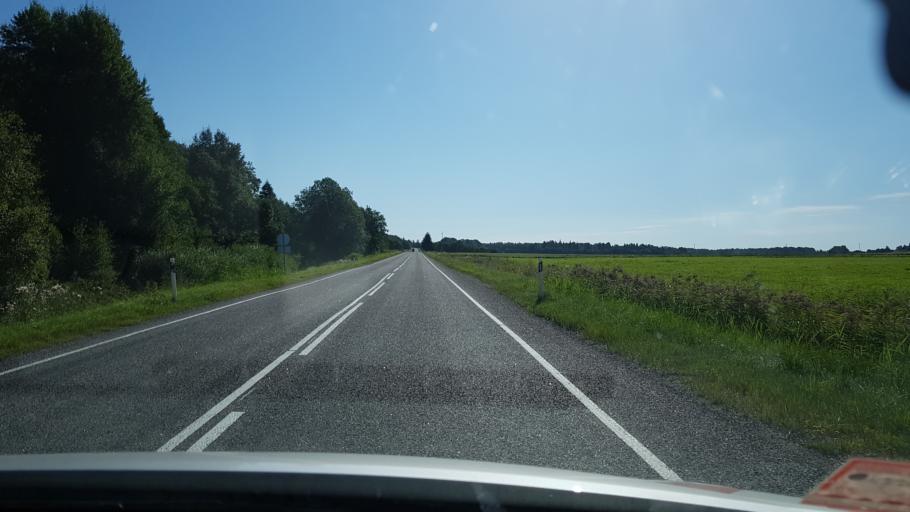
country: EE
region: Tartu
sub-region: Tartu linn
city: Tartu
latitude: 58.4686
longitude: 26.7279
